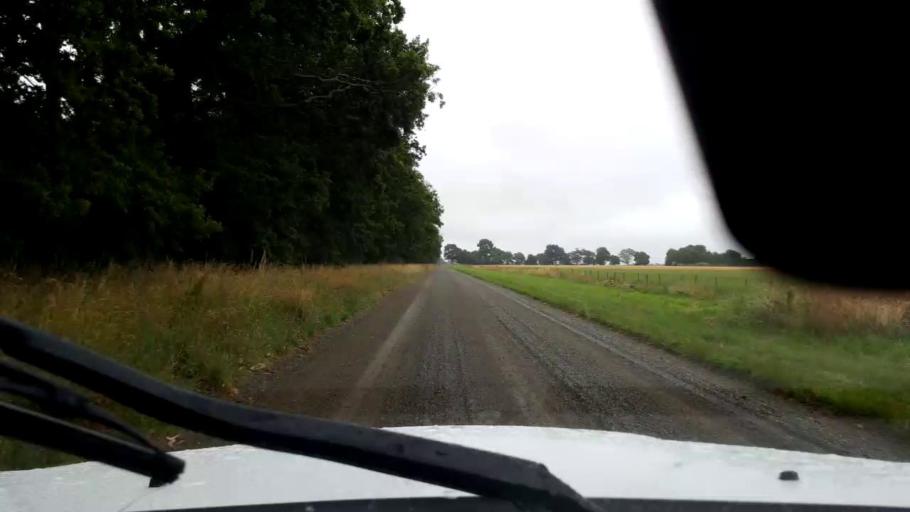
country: NZ
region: Canterbury
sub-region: Timaru District
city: Pleasant Point
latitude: -44.2033
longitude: 171.2814
